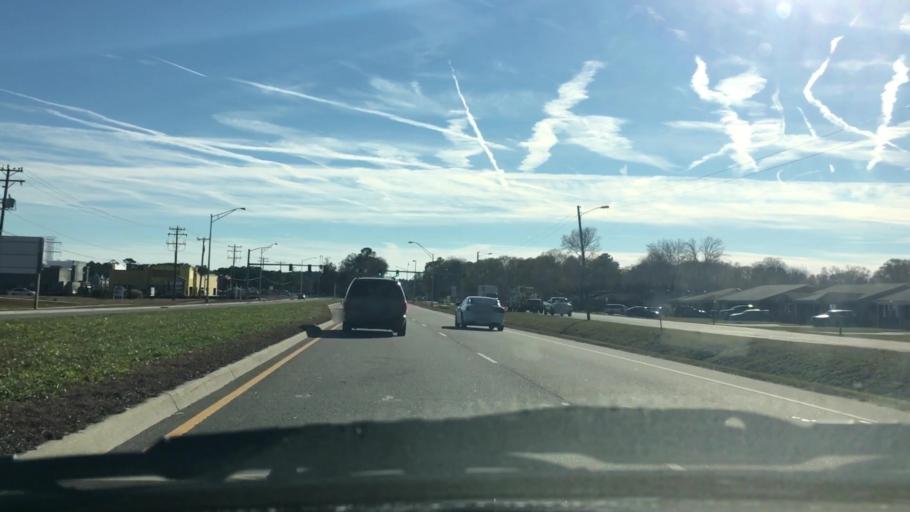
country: US
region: Virginia
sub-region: City of Portsmouth
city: Portsmouth Heights
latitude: 36.8758
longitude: -76.4232
